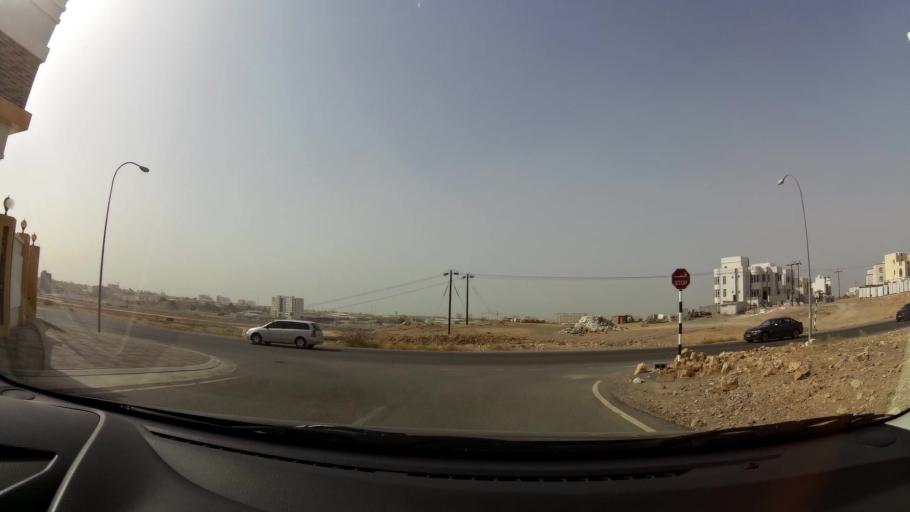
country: OM
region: Muhafazat Masqat
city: Bawshar
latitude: 23.5602
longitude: 58.3552
